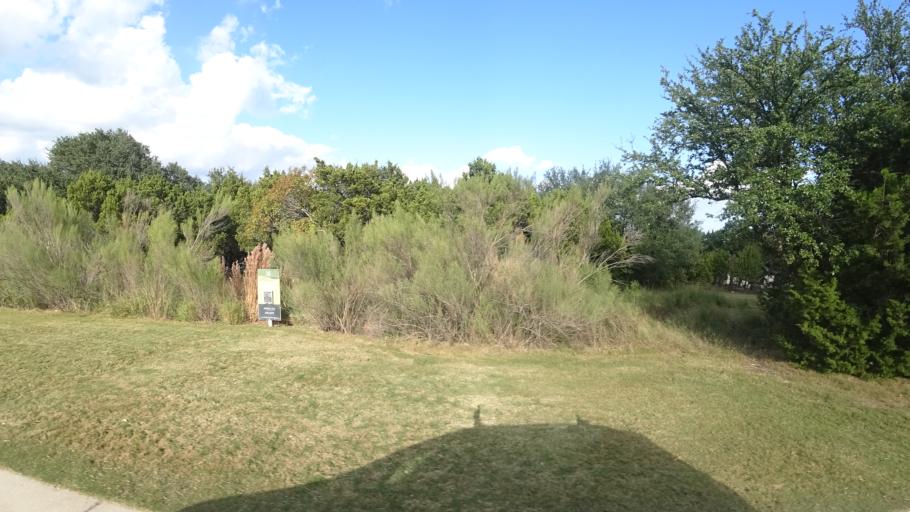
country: US
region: Texas
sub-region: Travis County
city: Barton Creek
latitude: 30.2731
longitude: -97.8791
